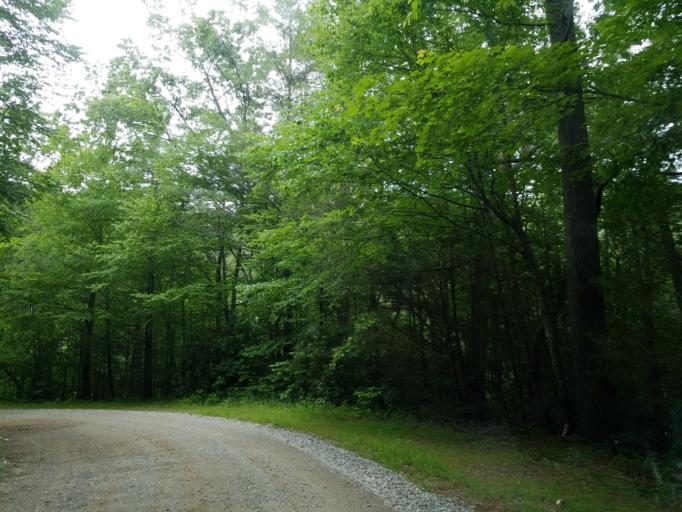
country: US
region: Georgia
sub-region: Union County
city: Blairsville
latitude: 34.7637
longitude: -84.0051
